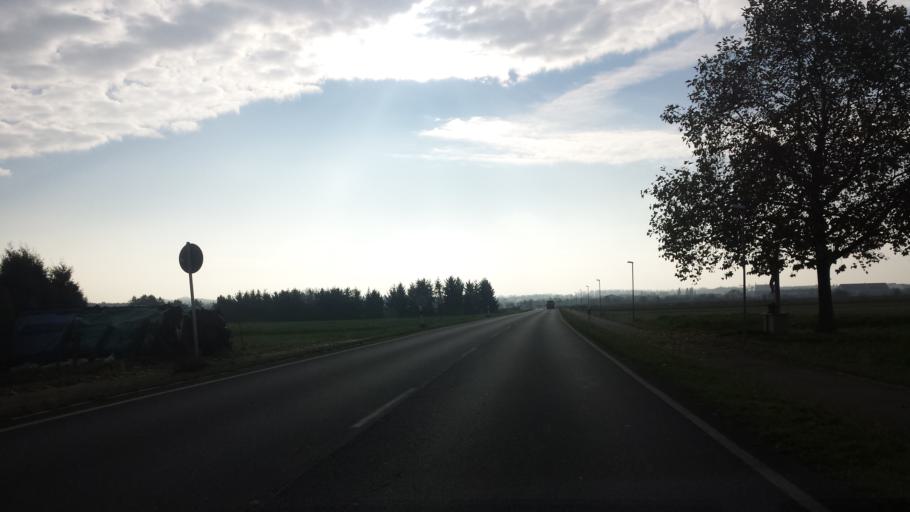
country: DE
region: Baden-Wuerttemberg
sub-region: Karlsruhe Region
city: Sankt Leon-Rot
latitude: 49.2571
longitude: 8.6396
